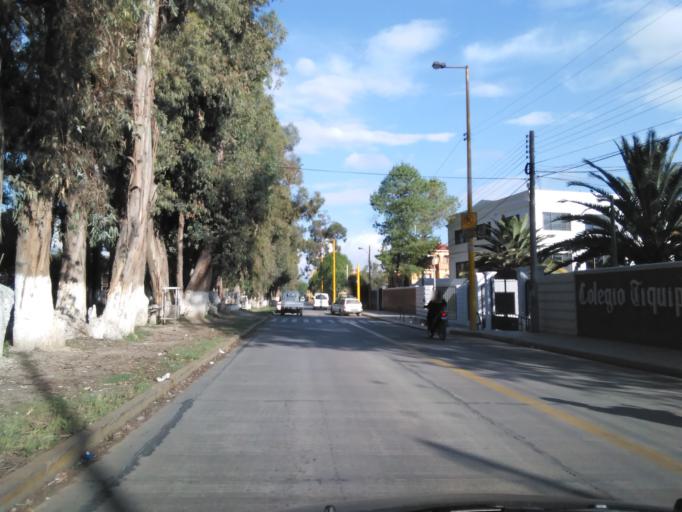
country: BO
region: Cochabamba
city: Cochabamba
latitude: -17.3439
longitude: -66.2078
